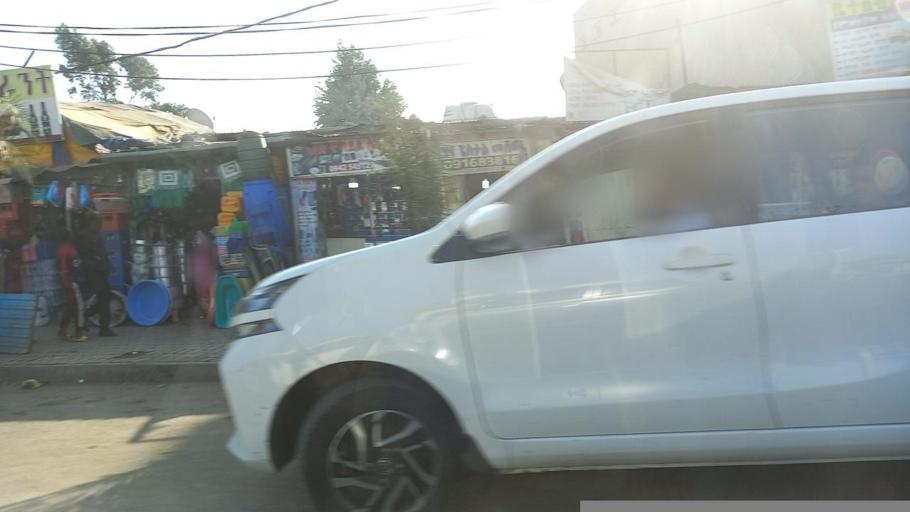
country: ET
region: Adis Abeba
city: Addis Ababa
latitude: 8.9305
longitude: 38.7427
